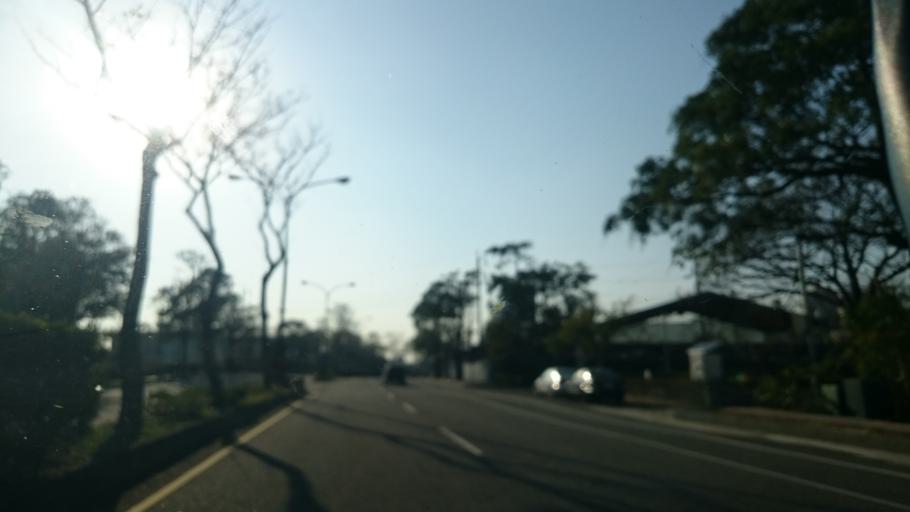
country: TW
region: Taiwan
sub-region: Miaoli
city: Miaoli
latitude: 24.6831
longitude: 120.8947
